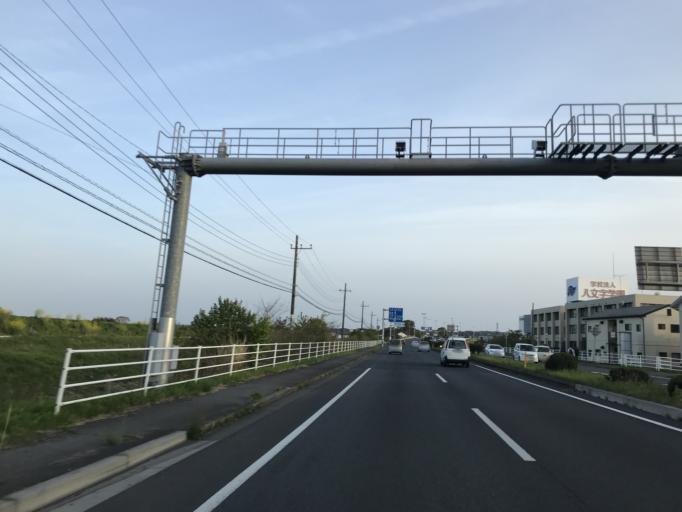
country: JP
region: Ibaraki
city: Katsuta
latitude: 36.3664
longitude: 140.5023
